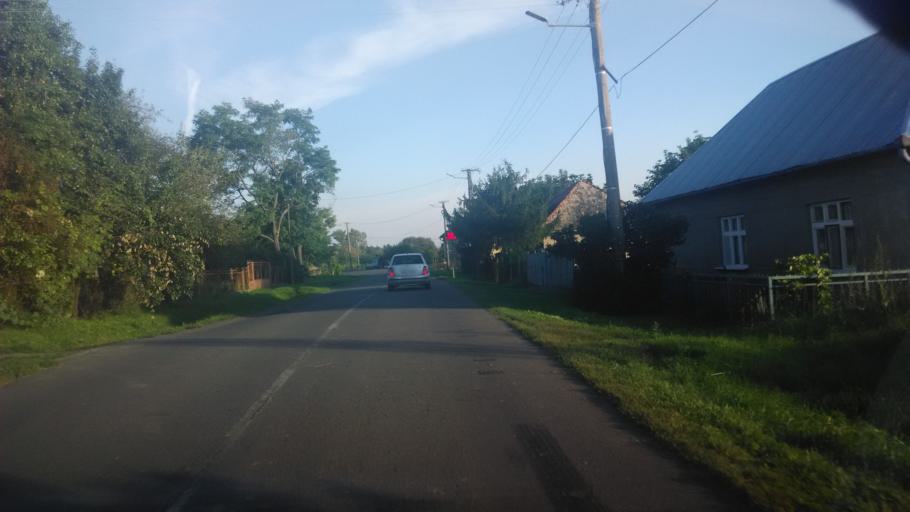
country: SK
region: Banskobystricky
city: Dudince
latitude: 48.1878
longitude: 18.8406
